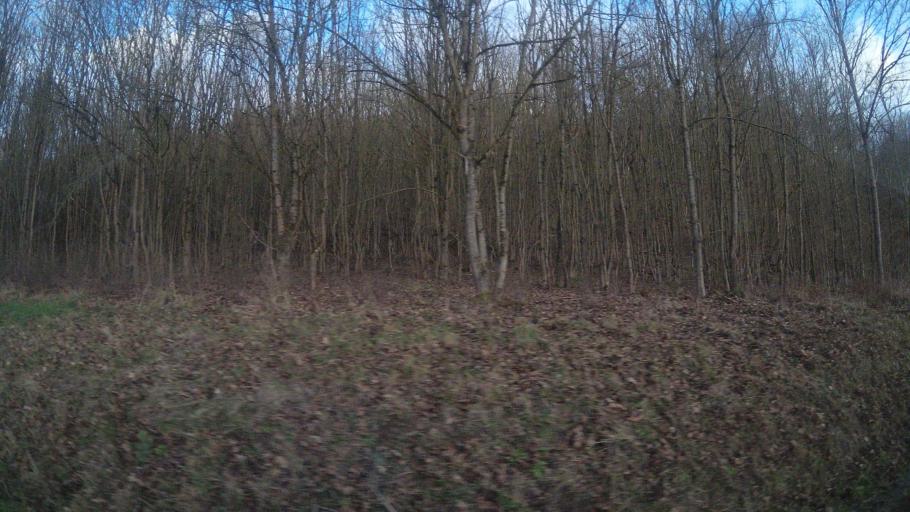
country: DE
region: Rheinland-Pfalz
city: Hochstatten
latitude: 49.7745
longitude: 7.8380
